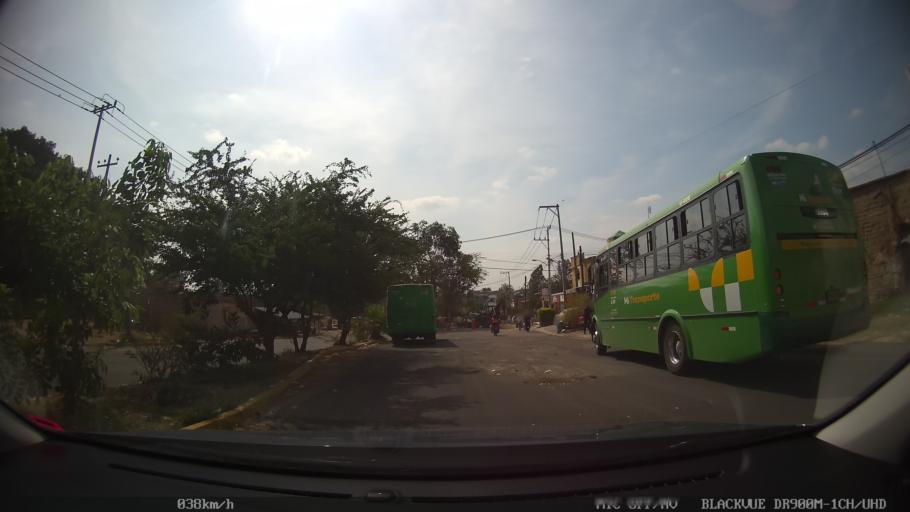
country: MX
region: Jalisco
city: Coyula
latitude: 20.6514
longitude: -103.2165
